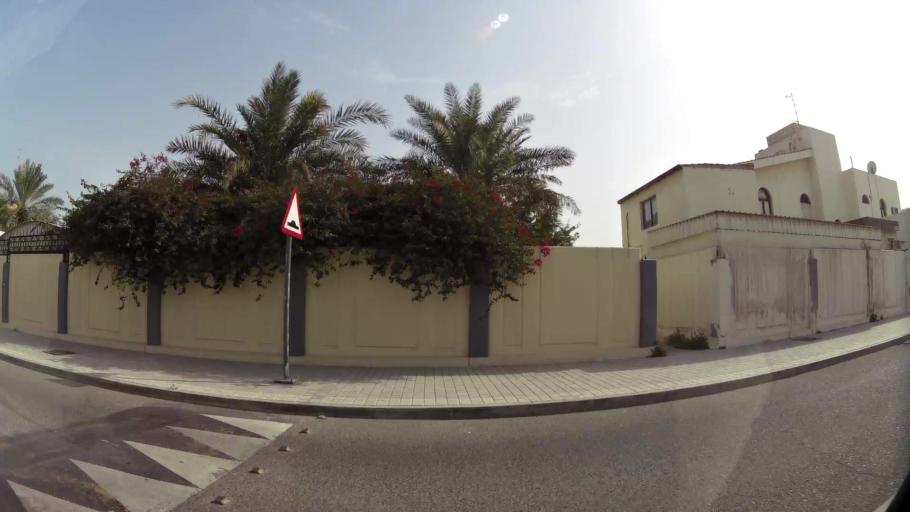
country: QA
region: Baladiyat ad Dawhah
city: Doha
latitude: 25.3247
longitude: 51.5050
